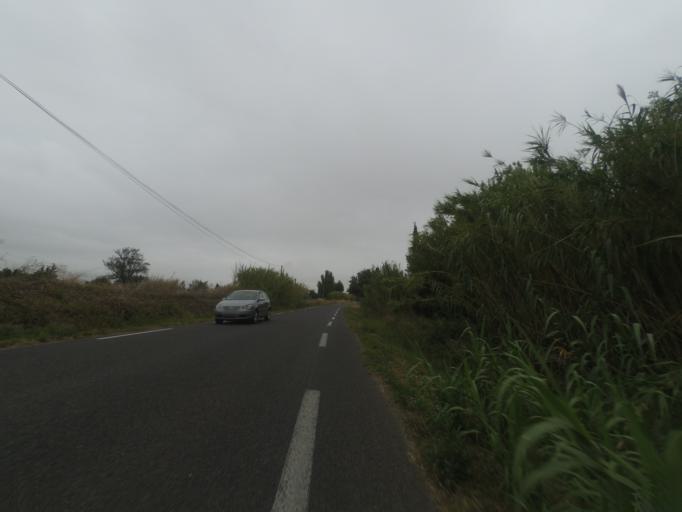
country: FR
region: Languedoc-Roussillon
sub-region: Departement des Pyrenees-Orientales
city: Pezilla-la-Riviere
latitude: 42.6938
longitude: 2.7815
